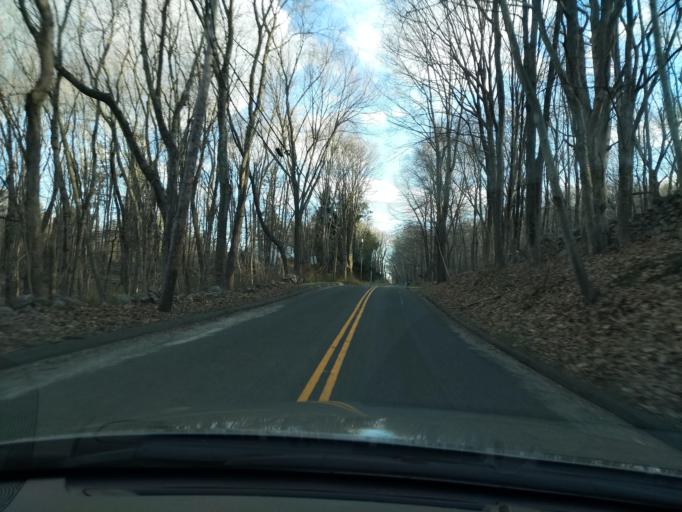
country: US
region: Connecticut
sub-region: Fairfield County
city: Newtown
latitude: 41.3742
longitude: -73.2826
